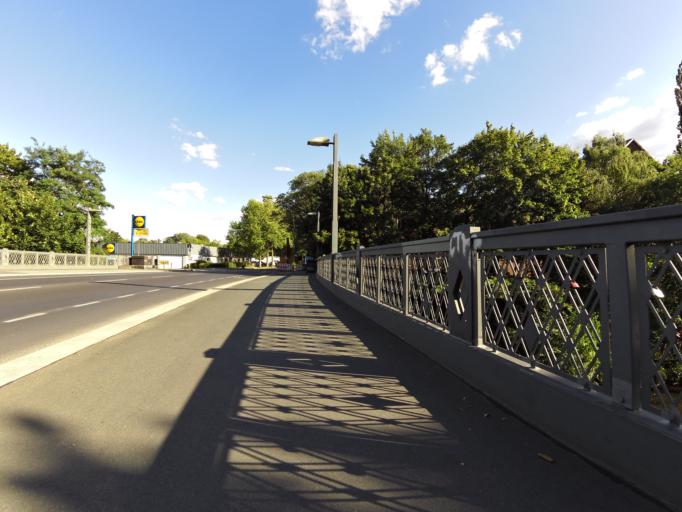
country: DE
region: Berlin
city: Steglitz Bezirk
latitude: 52.4450
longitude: 13.3304
